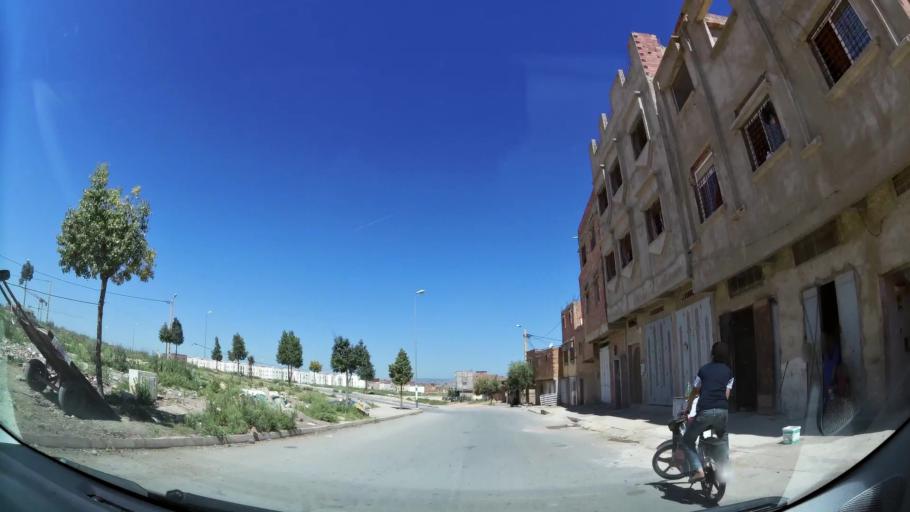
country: MA
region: Oriental
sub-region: Oujda-Angad
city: Oujda
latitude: 34.6560
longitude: -1.8773
